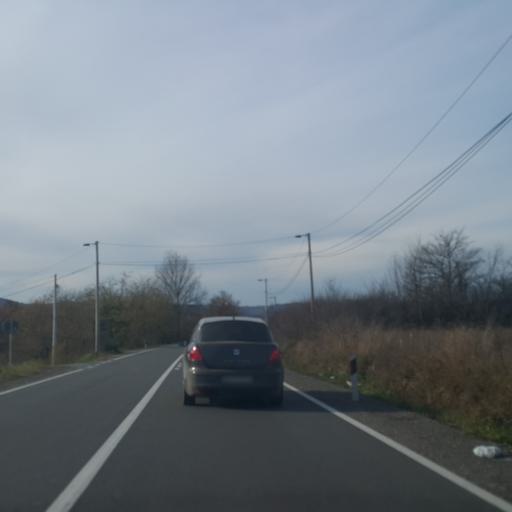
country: RS
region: Central Serbia
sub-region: Sumadijski Okrug
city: Arangelovac
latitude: 44.3371
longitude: 20.4279
